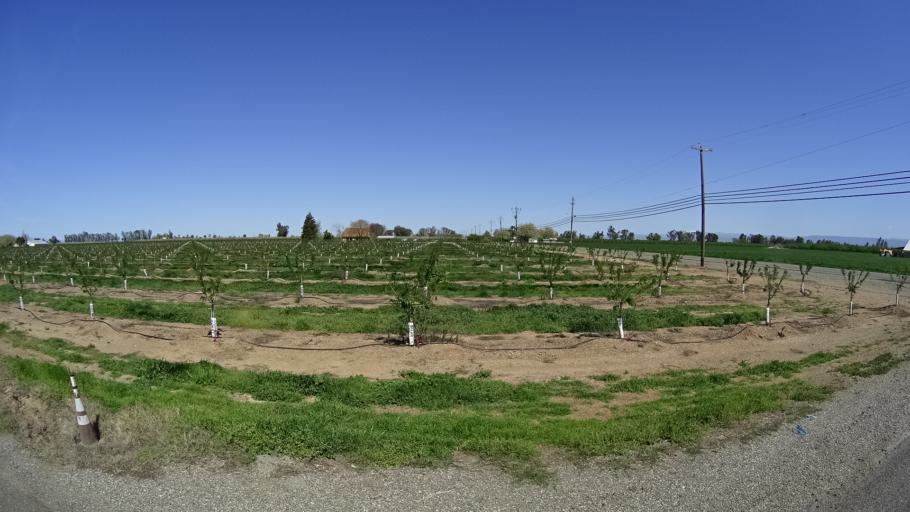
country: US
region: California
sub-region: Glenn County
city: Orland
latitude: 39.7897
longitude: -122.1044
